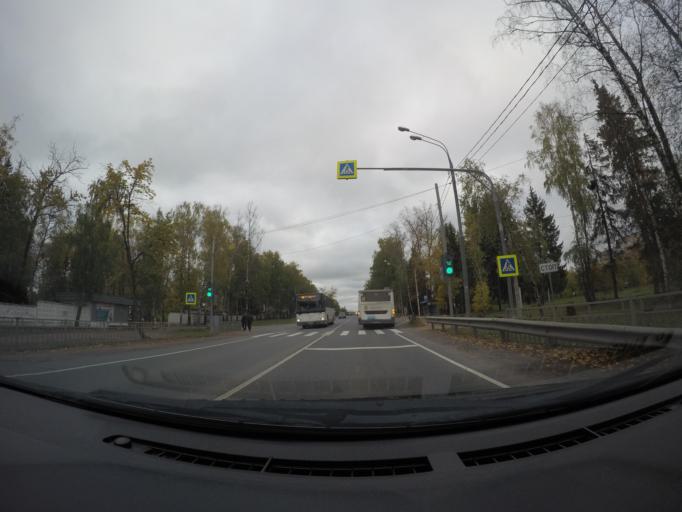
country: RU
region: Moskovskaya
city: Dorokhovo
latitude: 55.6300
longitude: 36.3363
